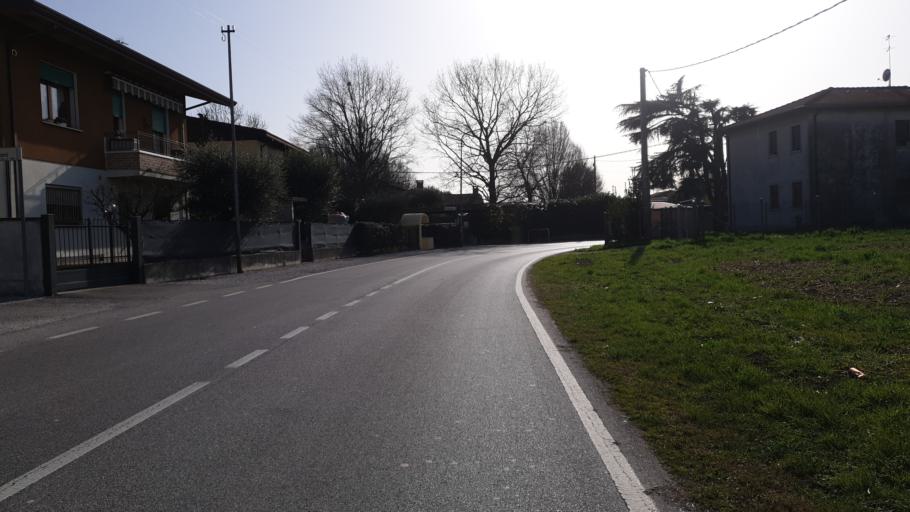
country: IT
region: Veneto
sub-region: Provincia di Padova
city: Vigodarzere
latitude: 45.4633
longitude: 11.8885
